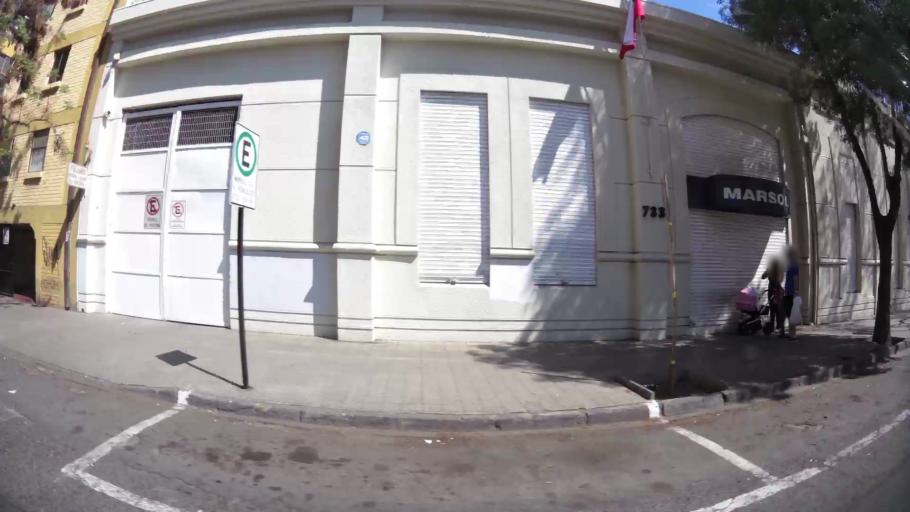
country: CL
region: Santiago Metropolitan
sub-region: Provincia de Santiago
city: Santiago
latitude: -33.4561
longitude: -70.6597
